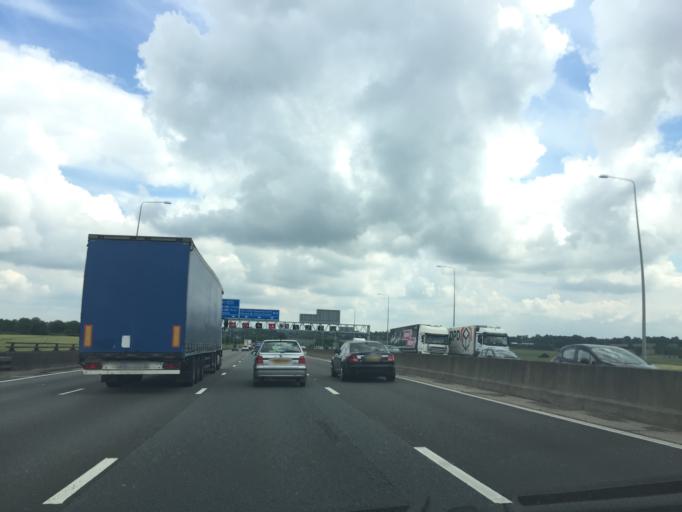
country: GB
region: England
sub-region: Hertfordshire
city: Shenley AV
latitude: 51.7052
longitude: -0.2518
